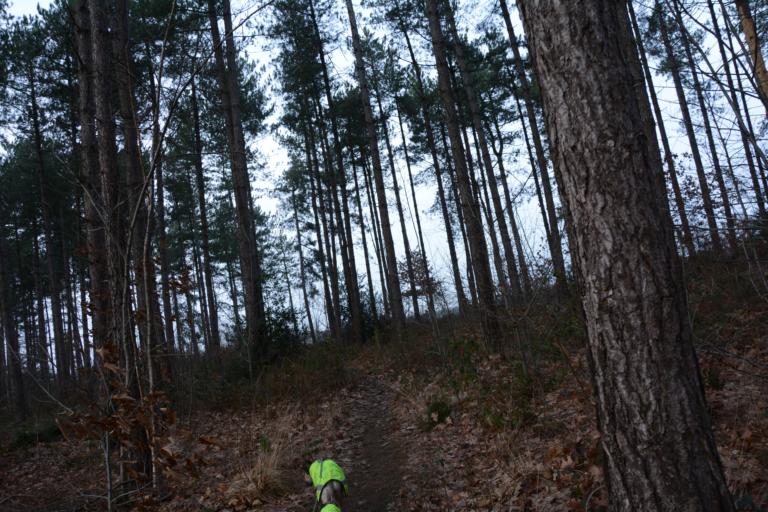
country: BE
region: Flanders
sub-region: Provincie Vlaams-Brabant
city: Scherpenheuvel-Zichem
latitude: 51.0405
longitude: 4.9387
